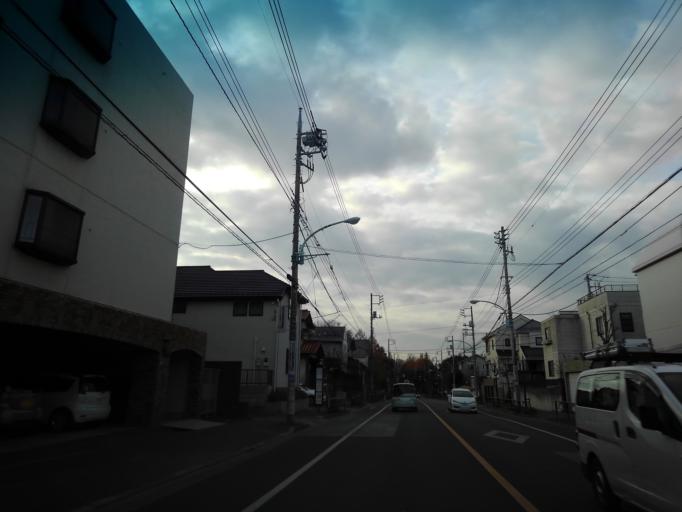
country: JP
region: Tokyo
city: Tanashicho
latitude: 35.7193
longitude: 139.5091
